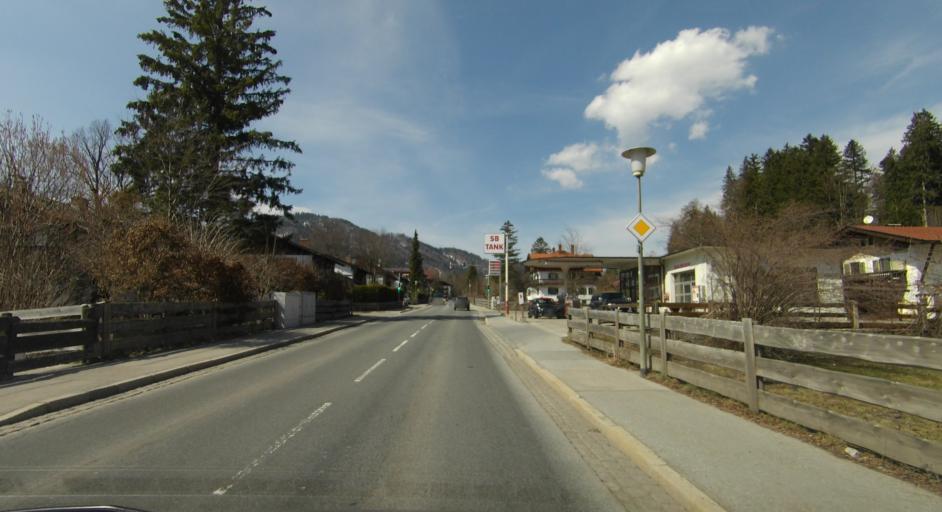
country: DE
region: Bavaria
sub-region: Upper Bavaria
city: Schliersee
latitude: 47.7029
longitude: 11.8824
